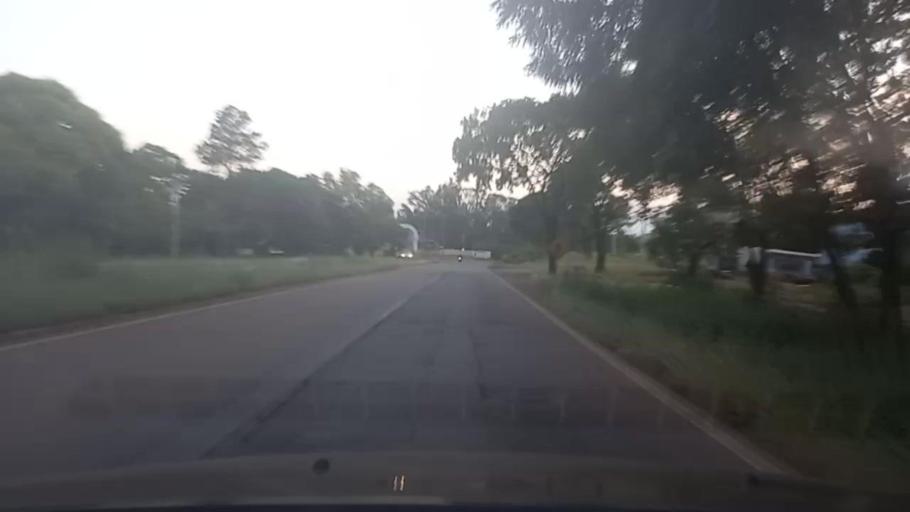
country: BR
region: Rio Grande do Sul
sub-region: Passo Fundo
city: Passo Fundo
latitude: -28.2880
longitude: -52.4544
